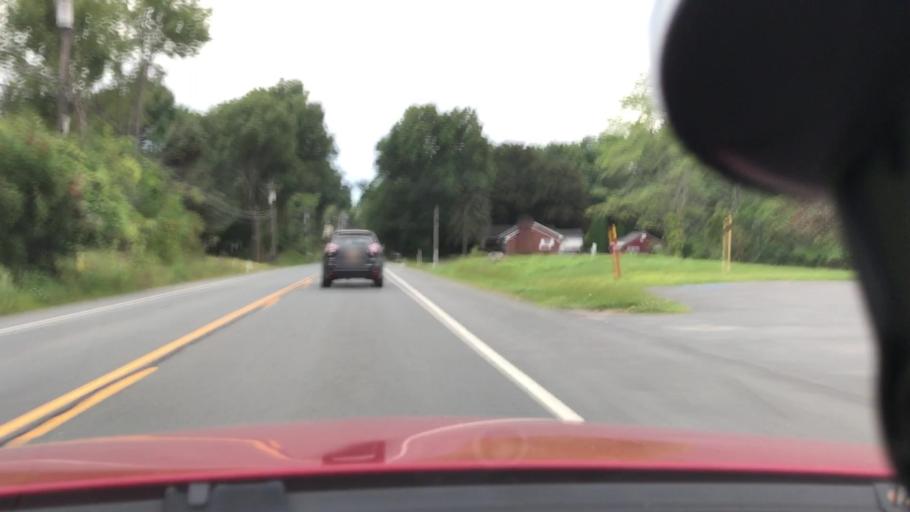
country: US
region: New York
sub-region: Albany County
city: Menands
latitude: 42.6871
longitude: -73.6881
